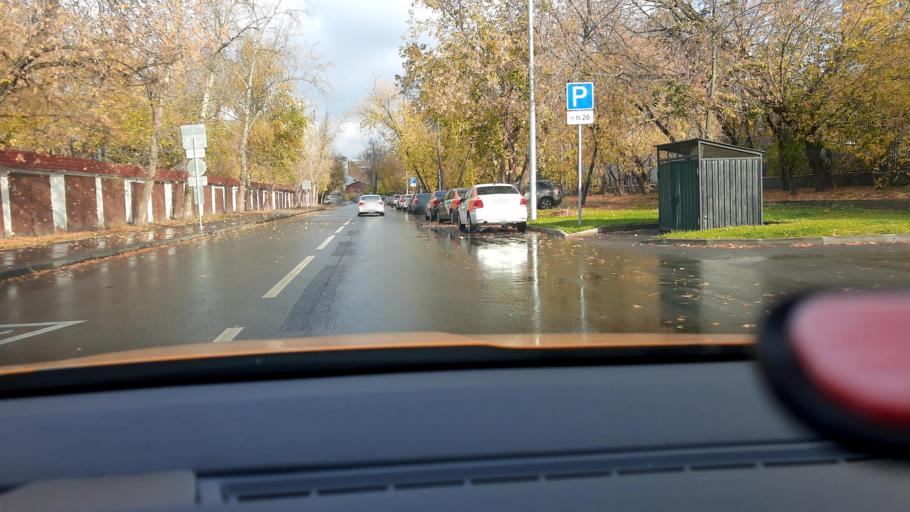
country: RU
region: Moscow
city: Lefortovo
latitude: 55.7750
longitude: 37.7322
